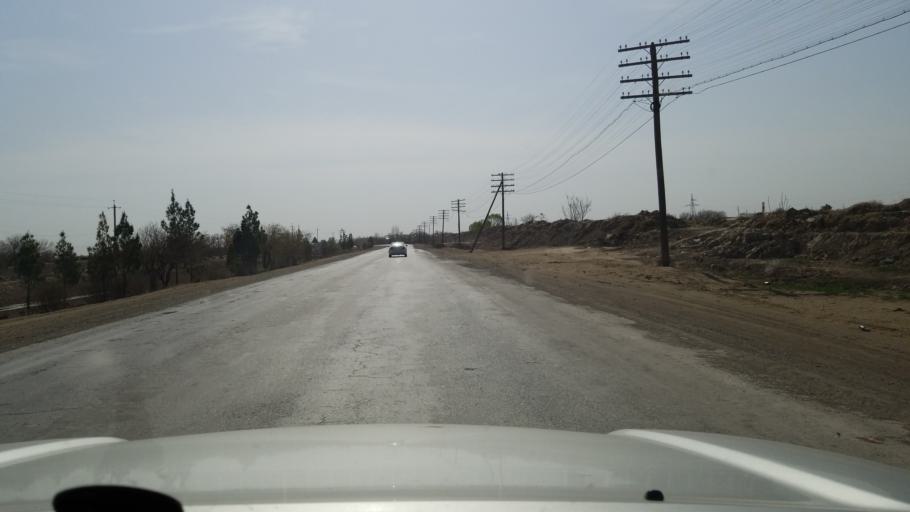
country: TM
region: Lebap
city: Sayat
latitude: 38.7977
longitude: 63.8549
